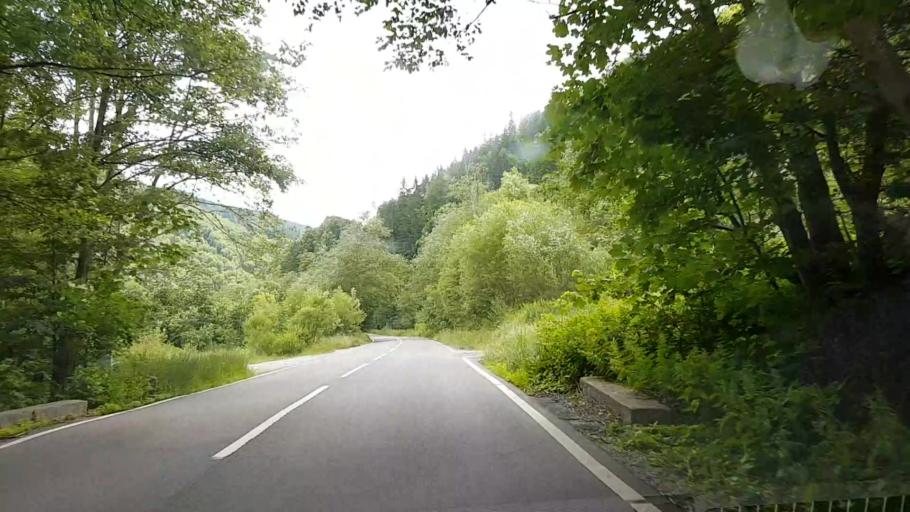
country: RO
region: Suceava
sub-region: Comuna Crucea
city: Crucea
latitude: 47.3272
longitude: 25.6212
